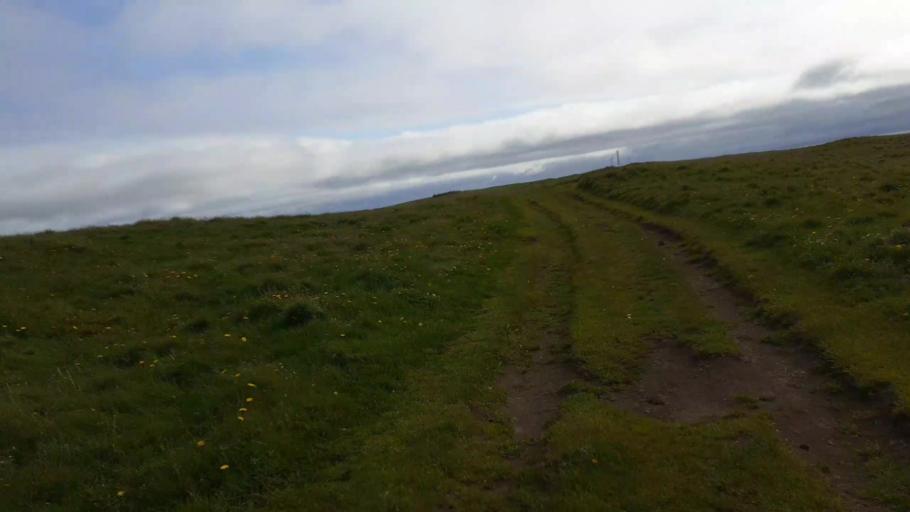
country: IS
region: Northeast
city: Dalvik
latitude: 66.5541
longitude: -18.0000
